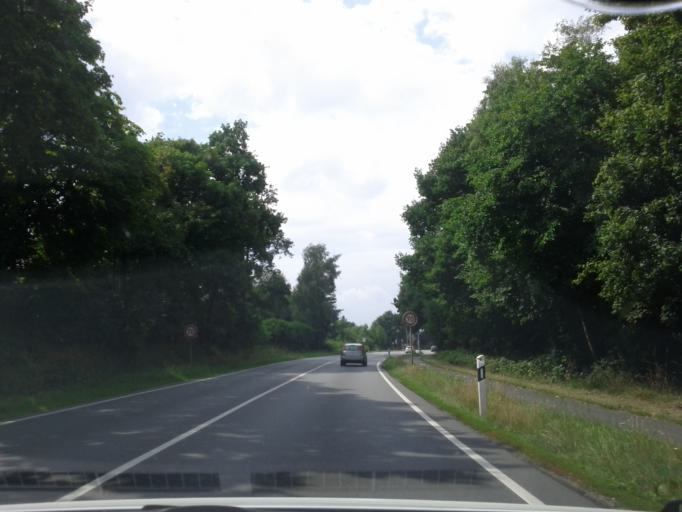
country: DE
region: Lower Saxony
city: Stade
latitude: 53.5855
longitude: 9.4609
